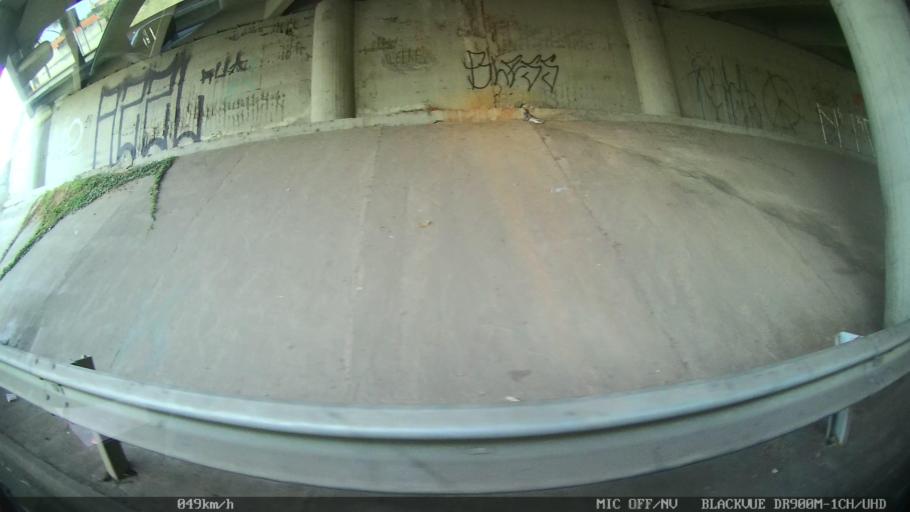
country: BR
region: Sao Paulo
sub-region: Piracicaba
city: Piracicaba
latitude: -22.7441
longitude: -47.6396
